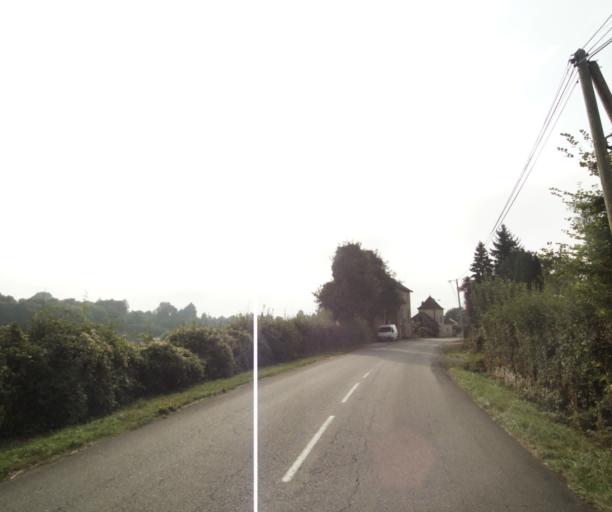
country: FR
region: Bourgogne
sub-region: Departement de Saone-et-Loire
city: Charolles
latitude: 46.4417
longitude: 4.2699
